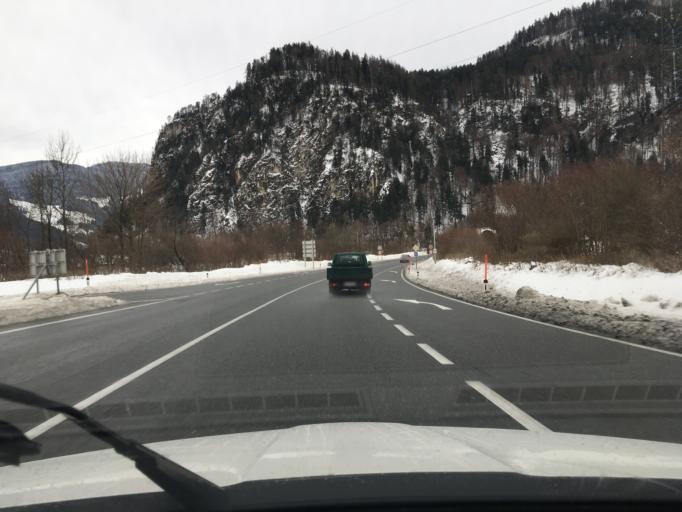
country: AT
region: Tyrol
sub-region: Politischer Bezirk Schwaz
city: Strass im Zillertal
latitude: 47.3971
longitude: 11.8080
